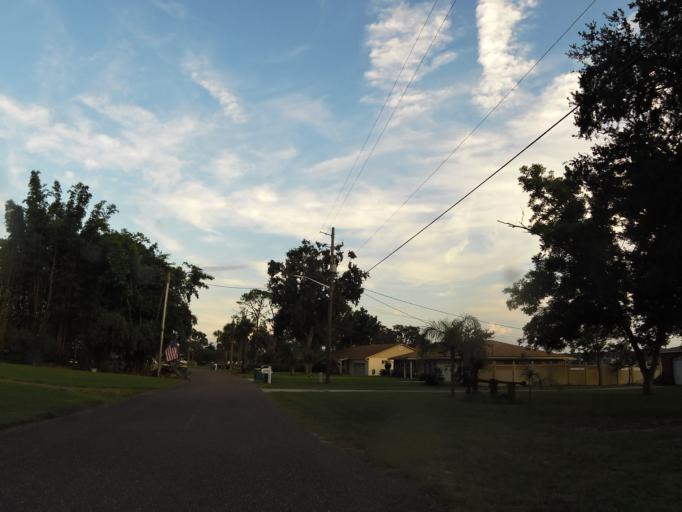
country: US
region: Florida
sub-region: Duval County
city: Atlantic Beach
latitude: 30.3955
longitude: -81.5033
